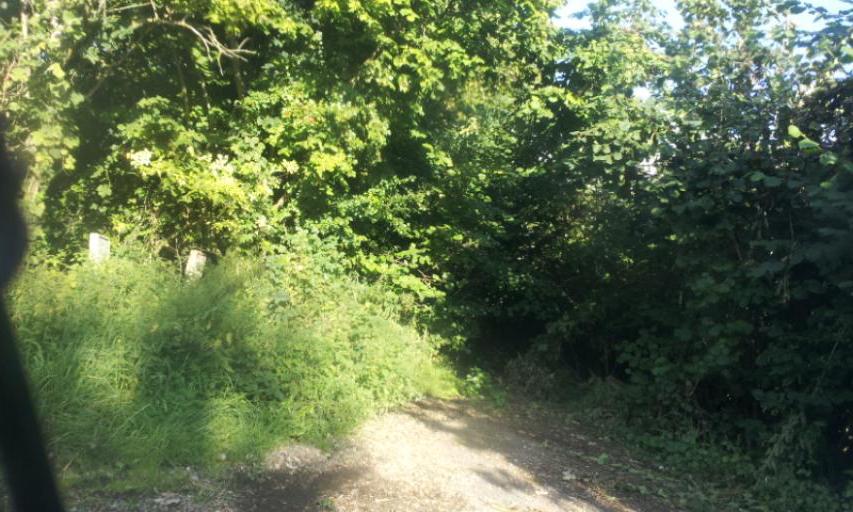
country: GB
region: England
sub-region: Kent
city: Kings Hill
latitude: 51.2673
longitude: 0.3885
